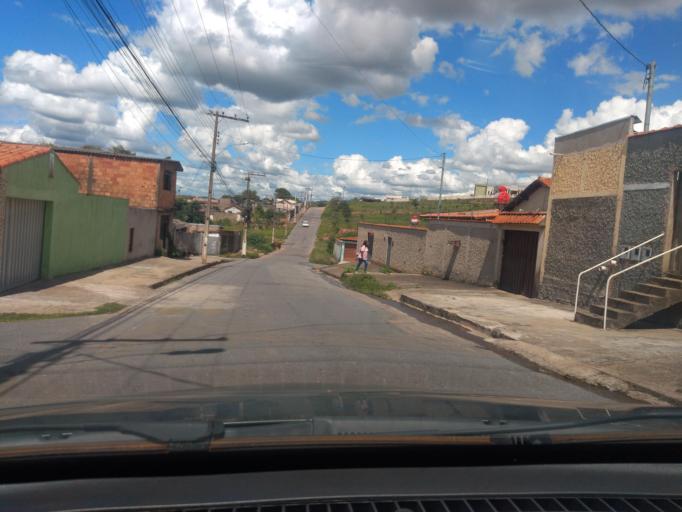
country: BR
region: Minas Gerais
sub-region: Tres Coracoes
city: Tres Coracoes
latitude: -21.6828
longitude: -45.2471
